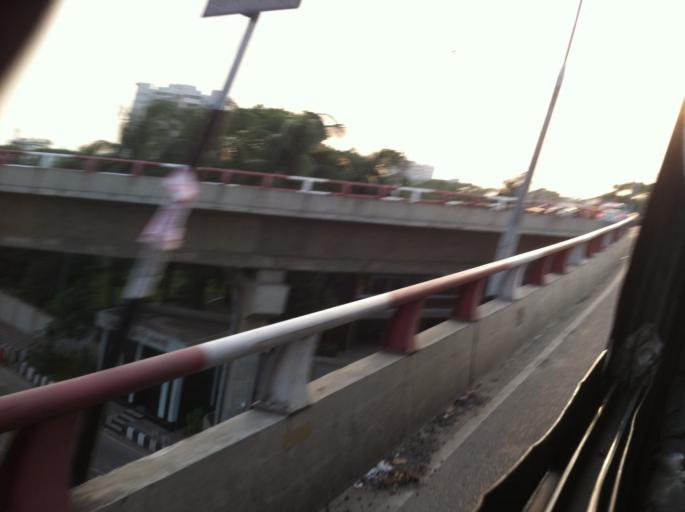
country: BD
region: Dhaka
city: Tungi
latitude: 23.8159
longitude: 90.4051
